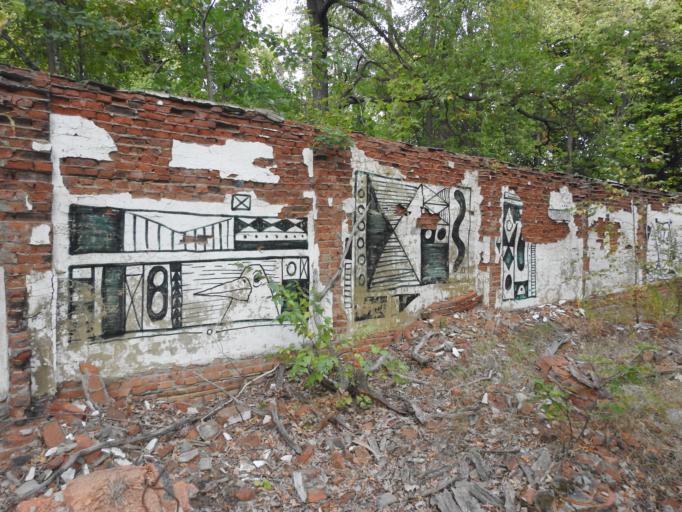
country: RU
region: Saratov
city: Sokolovyy
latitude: 51.5510
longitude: 45.8664
